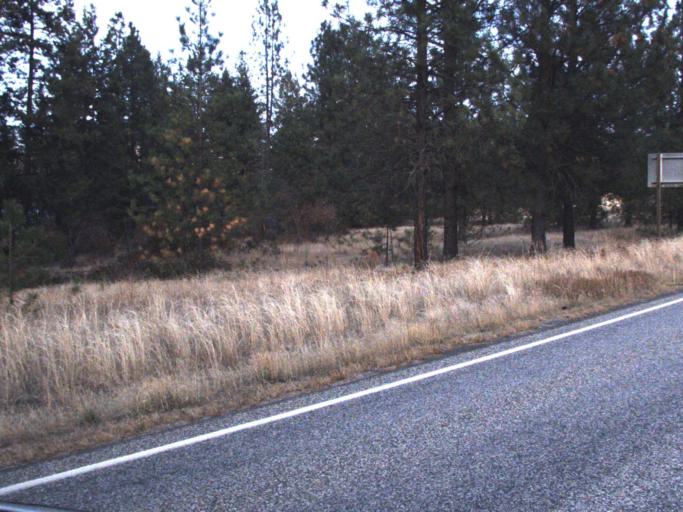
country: US
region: Washington
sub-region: Stevens County
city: Kettle Falls
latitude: 48.8097
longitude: -117.9468
